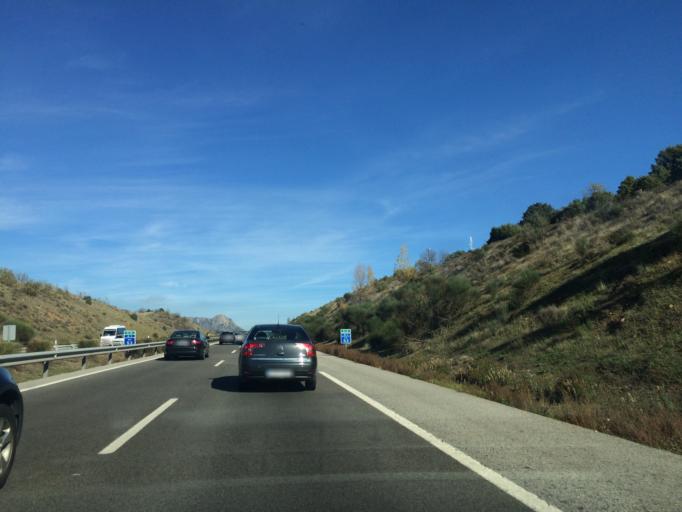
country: ES
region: Madrid
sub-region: Provincia de Madrid
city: Cabanillas de la Sierra
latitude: 40.8152
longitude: -3.6162
